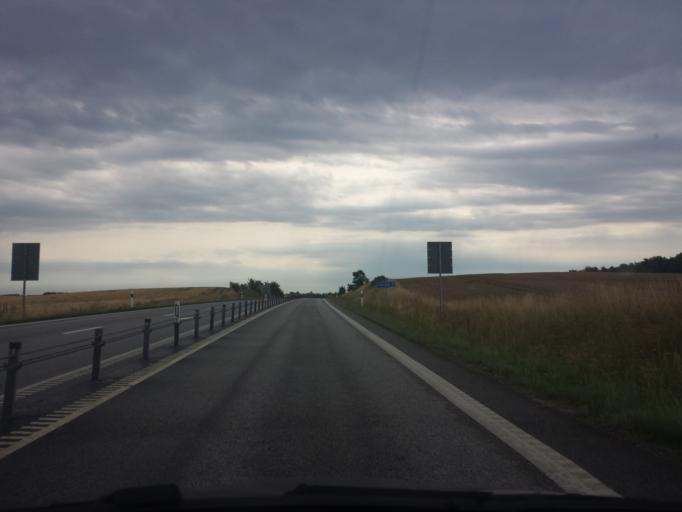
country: SE
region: Skane
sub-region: Ystads Kommun
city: Ystad
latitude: 55.4677
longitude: 13.7098
